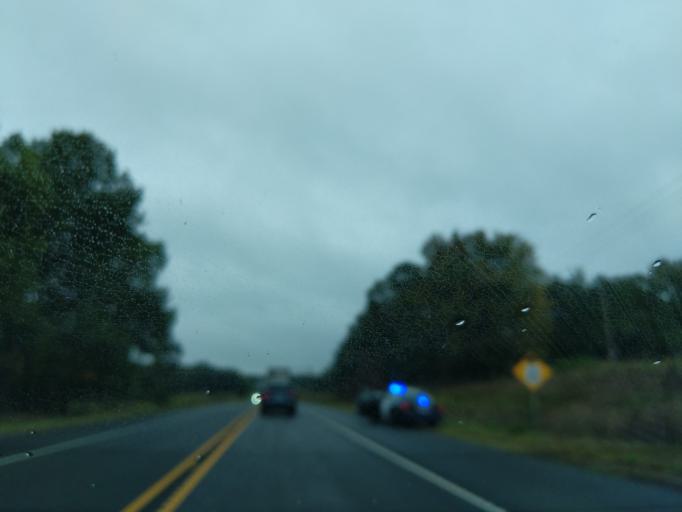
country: US
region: Louisiana
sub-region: Caddo Parish
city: Greenwood
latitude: 32.4377
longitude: -93.9832
